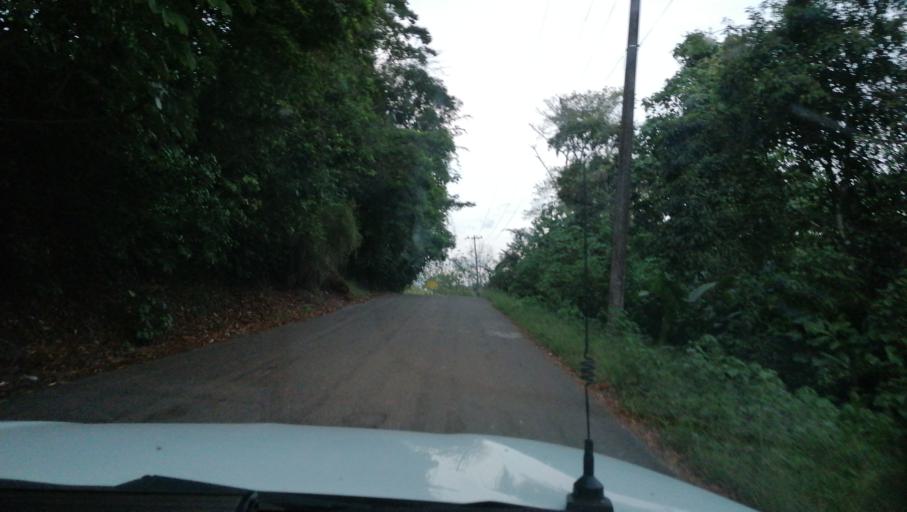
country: MX
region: Chiapas
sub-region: Ostuacan
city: Nuevo Juan del Grijalva
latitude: 17.4445
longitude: -93.3539
